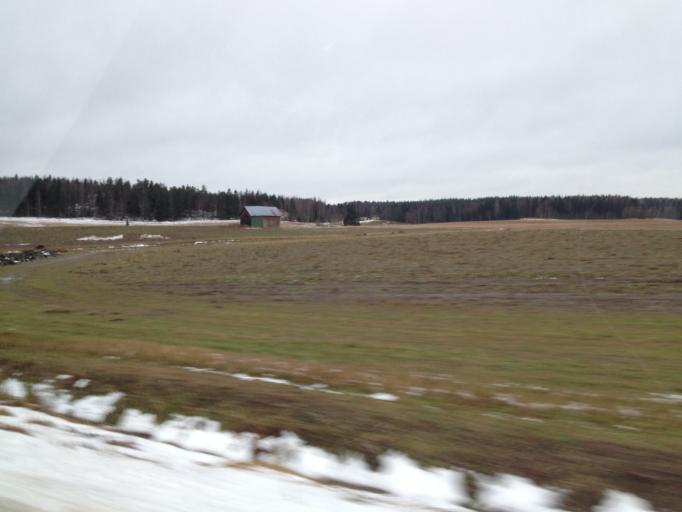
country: FI
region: Uusimaa
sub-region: Raaseporin
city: Karis
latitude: 60.0905
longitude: 23.7803
